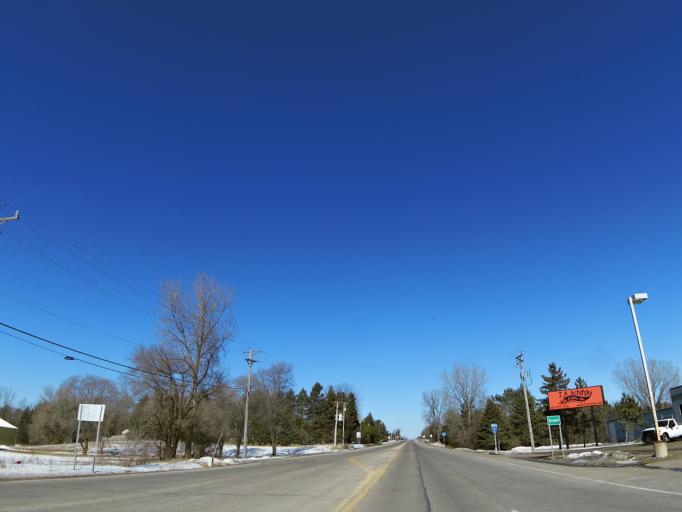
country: US
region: Minnesota
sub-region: Washington County
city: Lake Elmo
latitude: 45.0363
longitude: -92.8834
